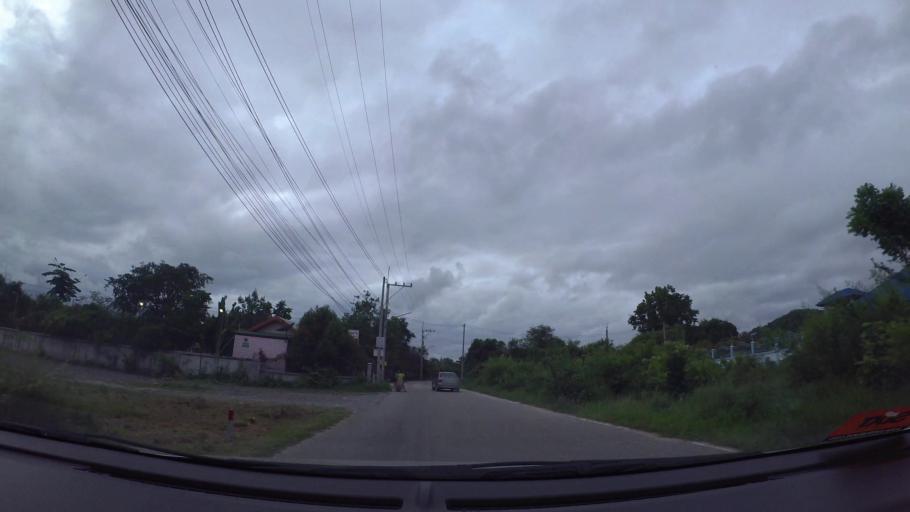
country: TH
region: Chon Buri
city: Sattahip
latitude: 12.6948
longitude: 100.9017
